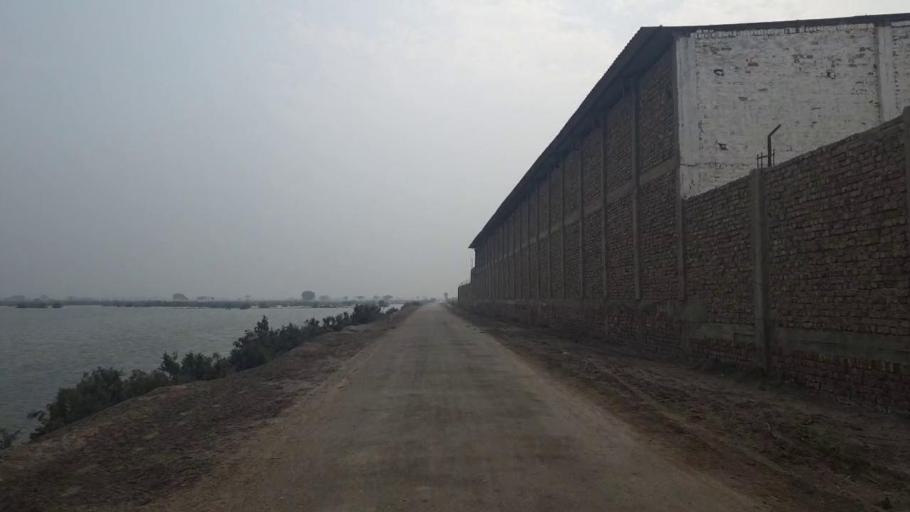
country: PK
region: Sindh
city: Tando Adam
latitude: 25.7928
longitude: 68.7086
